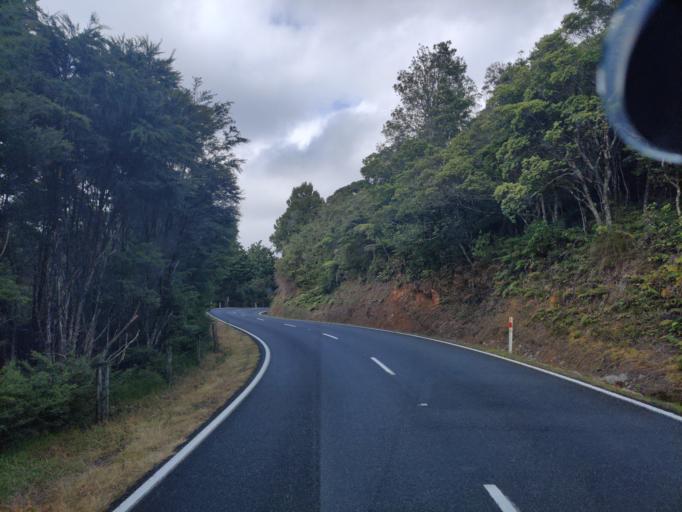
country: NZ
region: Northland
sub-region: Whangarei
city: Ngunguru
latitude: -35.5789
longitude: 174.4119
